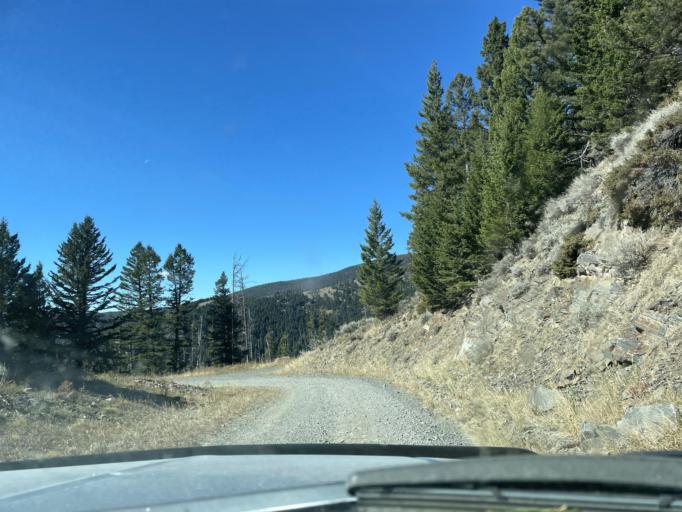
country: US
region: Montana
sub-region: Broadwater County
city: Townsend
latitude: 46.5096
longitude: -111.2845
